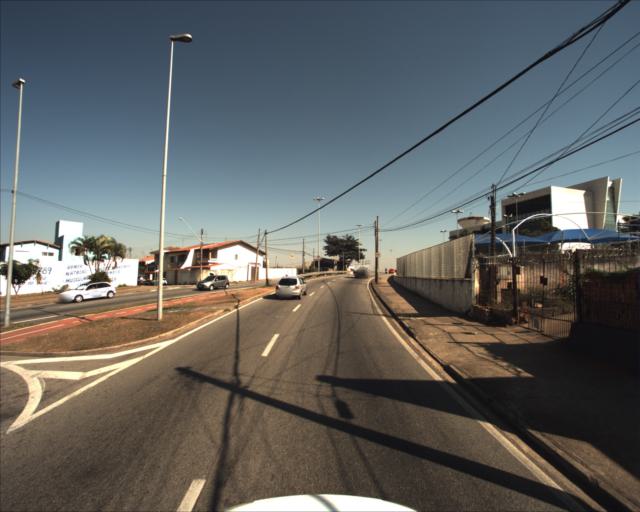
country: BR
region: Sao Paulo
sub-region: Sorocaba
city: Sorocaba
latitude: -23.4879
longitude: -47.4786
